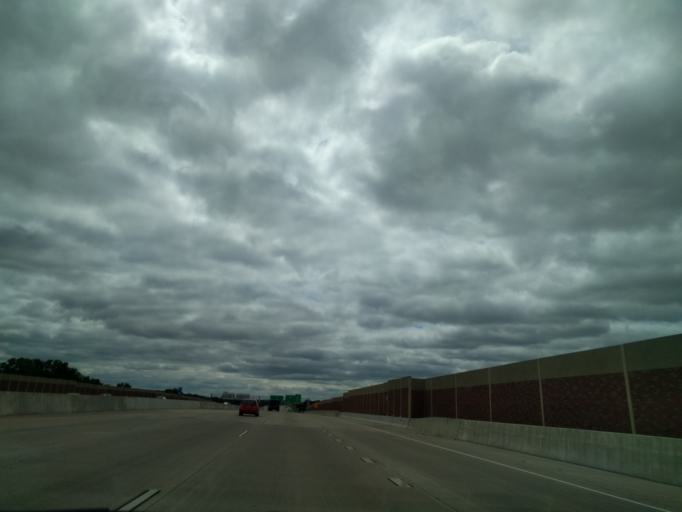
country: US
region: Wisconsin
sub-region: Brown County
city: Ashwaubenon
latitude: 44.4959
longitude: -88.0817
